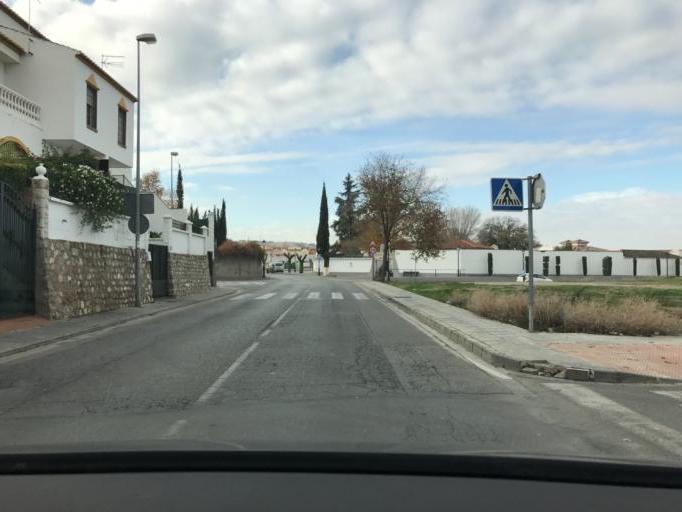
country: ES
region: Andalusia
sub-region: Provincia de Granada
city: Ogijares
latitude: 37.1248
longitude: -3.6083
